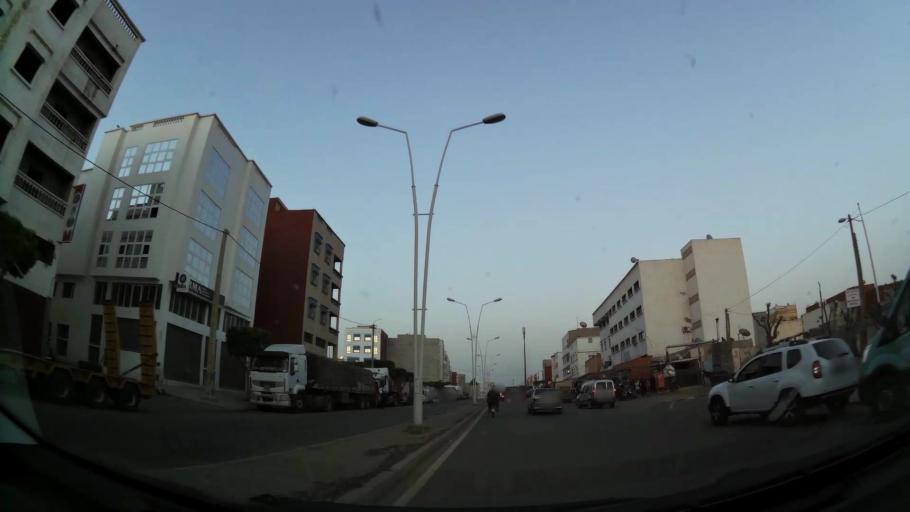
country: MA
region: Souss-Massa-Draa
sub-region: Inezgane-Ait Mellou
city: Inezgane
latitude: 30.3785
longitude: -9.5024
